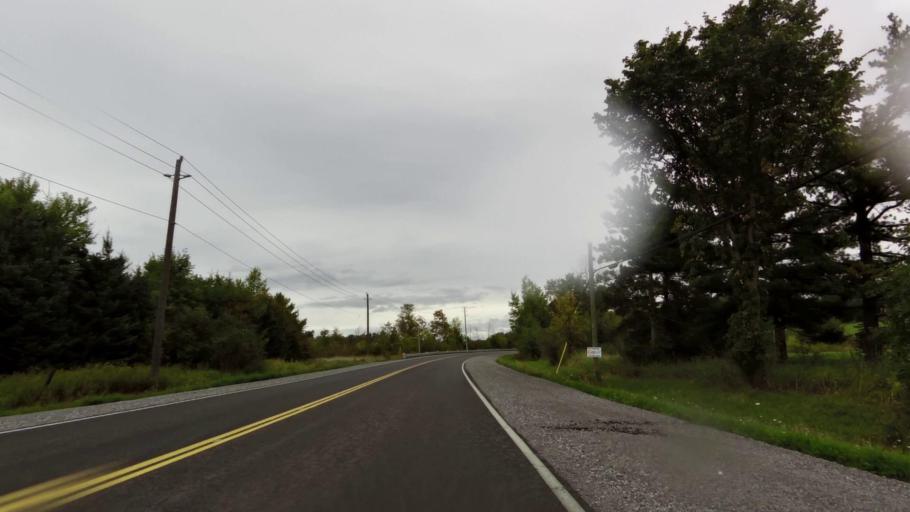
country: CA
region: Ontario
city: Bells Corners
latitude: 45.1548
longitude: -75.6341
